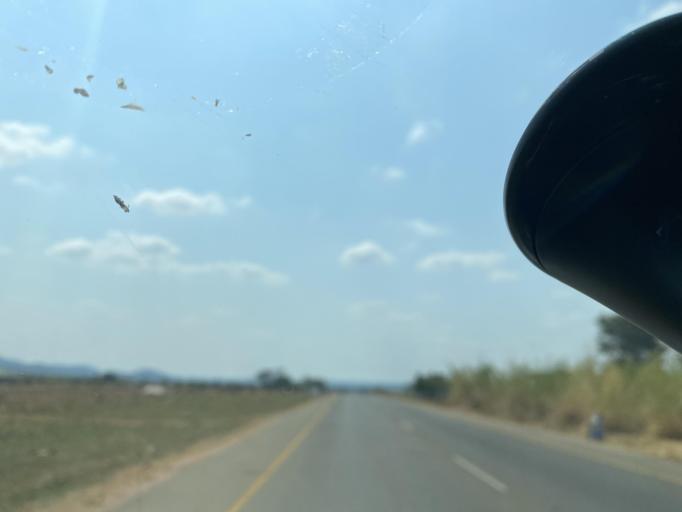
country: ZM
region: Lusaka
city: Chongwe
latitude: -15.5758
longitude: 28.7005
